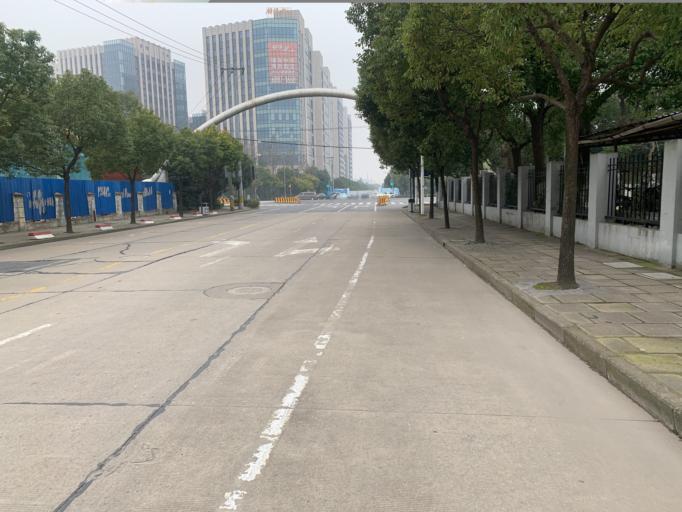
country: CN
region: Shanghai Shi
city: Huamu
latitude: 31.2485
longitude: 121.6220
